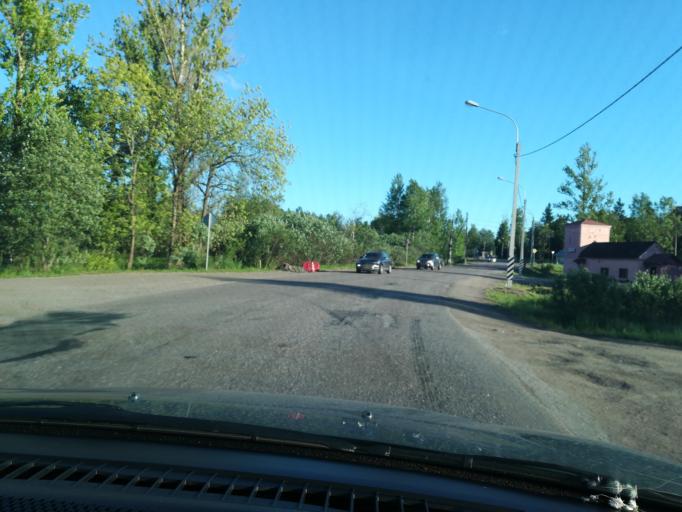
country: RU
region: Leningrad
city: Lesogorskiy
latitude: 61.0466
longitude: 28.9276
